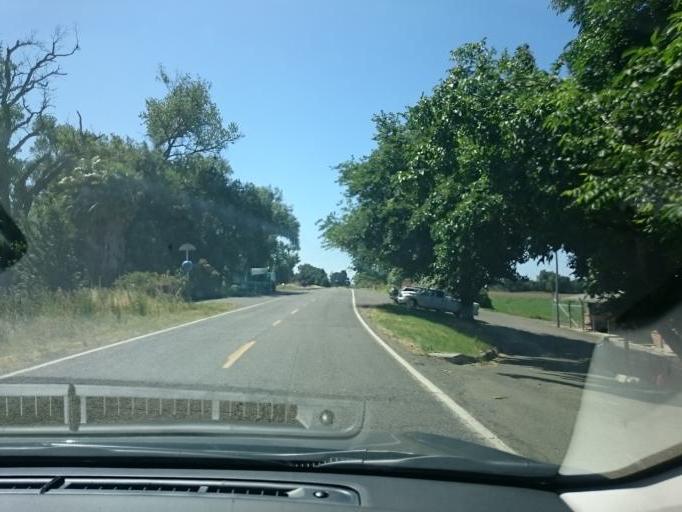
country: US
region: California
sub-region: Sacramento County
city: Parkway
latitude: 38.4861
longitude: -121.5533
